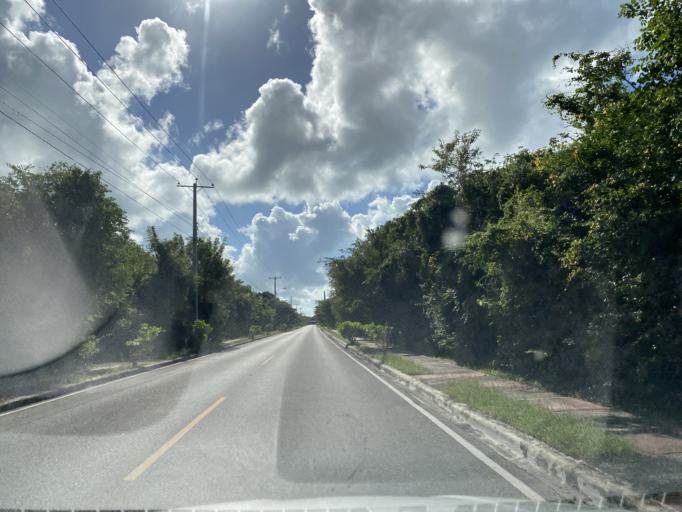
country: DO
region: La Altagracia
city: San Rafael del Yuma
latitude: 18.3374
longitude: -68.8105
